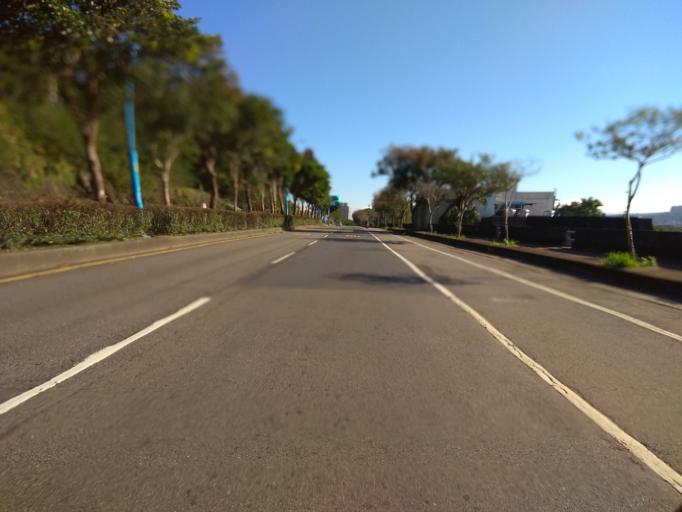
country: TW
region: Taiwan
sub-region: Hsinchu
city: Zhubei
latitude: 24.8996
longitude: 121.1195
